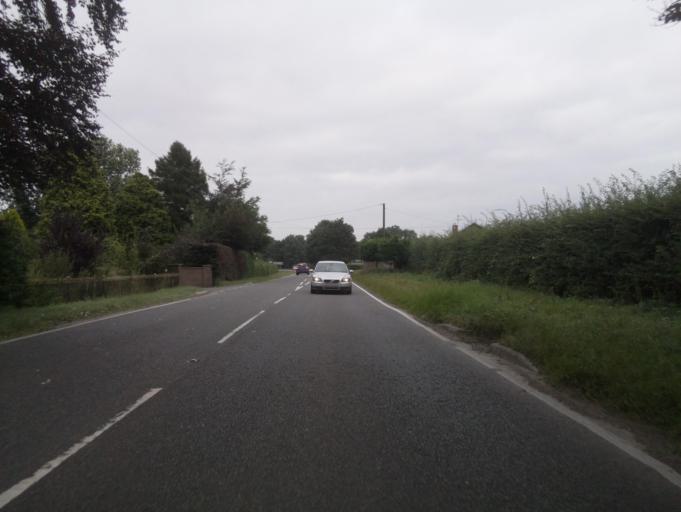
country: GB
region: England
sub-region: Shropshire
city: Astley
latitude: 52.7628
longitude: -2.6837
